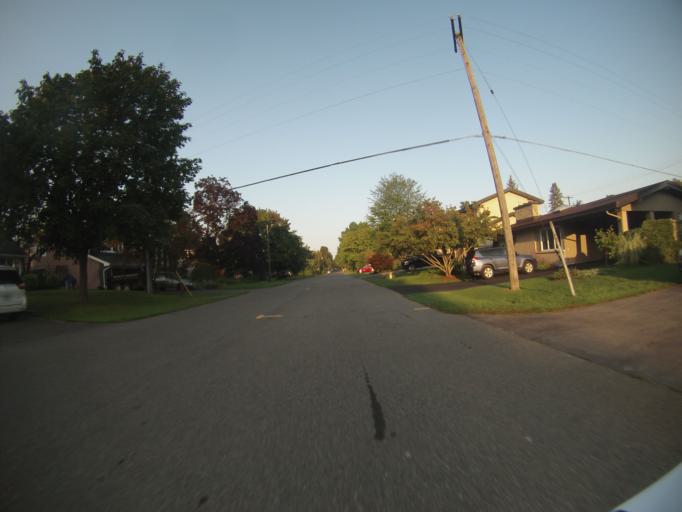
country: CA
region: Ontario
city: Ottawa
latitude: 45.3966
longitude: -75.6534
